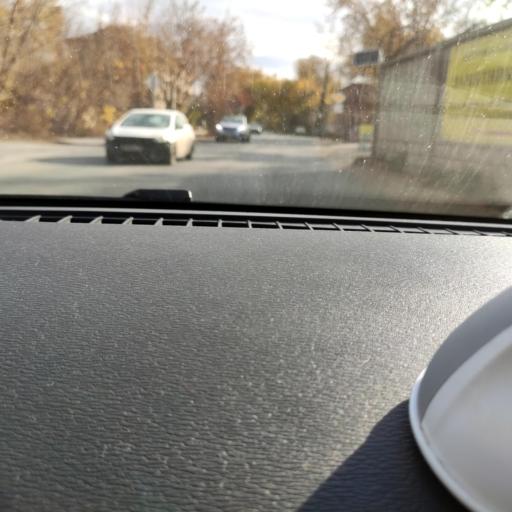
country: RU
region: Samara
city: Samara
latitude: 53.2184
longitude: 50.1965
